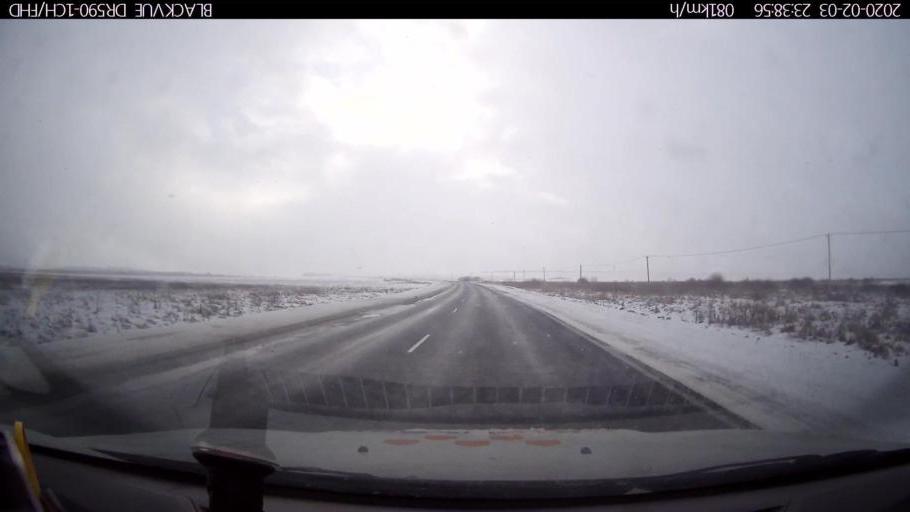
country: RU
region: Nizjnij Novgorod
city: Dal'neye Konstantinovo
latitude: 55.8892
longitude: 44.1433
